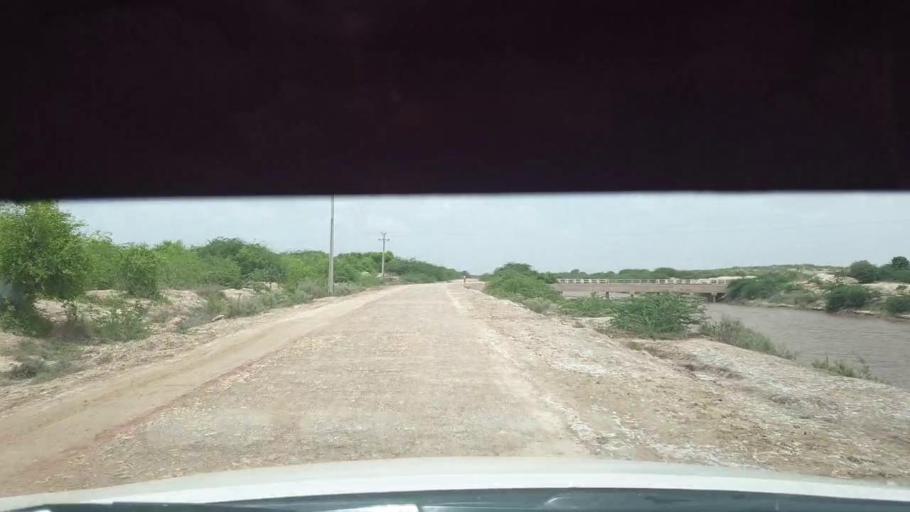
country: PK
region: Sindh
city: Kadhan
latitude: 24.5299
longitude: 69.1266
